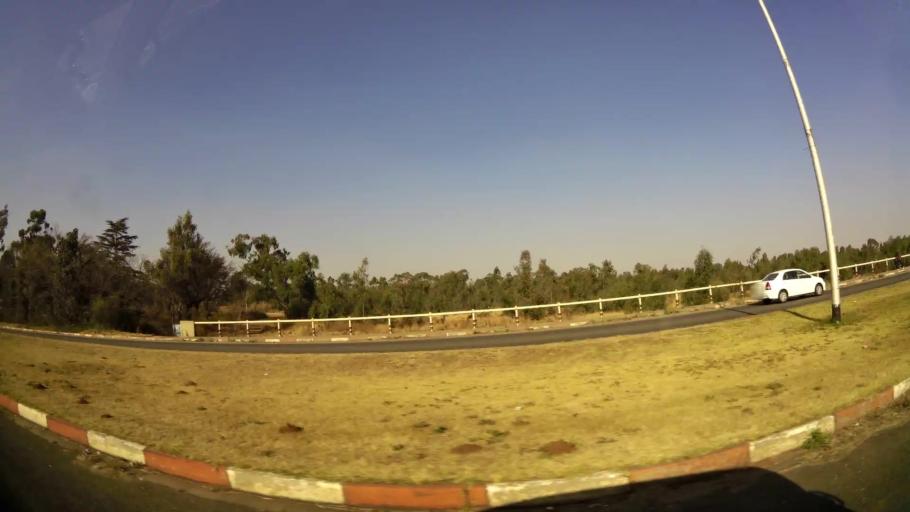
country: ZA
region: Gauteng
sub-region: West Rand District Municipality
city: Randfontein
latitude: -26.1610
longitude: 27.7143
